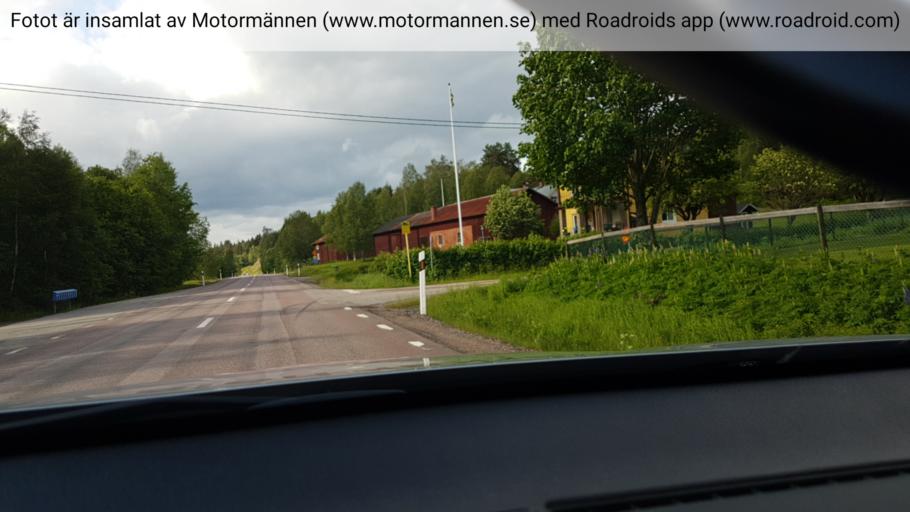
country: SE
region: Vaermland
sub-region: Torsby Kommun
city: Torsby
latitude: 60.5718
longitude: 13.0879
